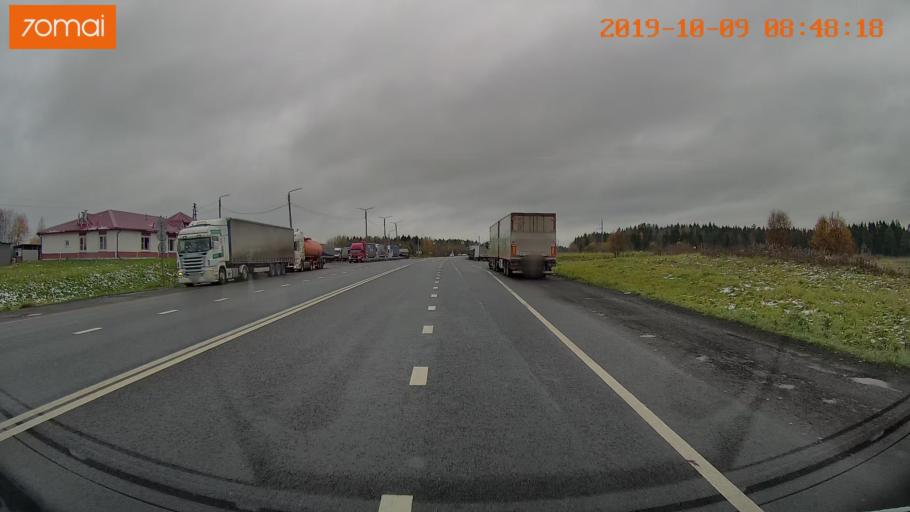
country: RU
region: Vologda
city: Vologda
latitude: 59.0722
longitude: 40.0283
